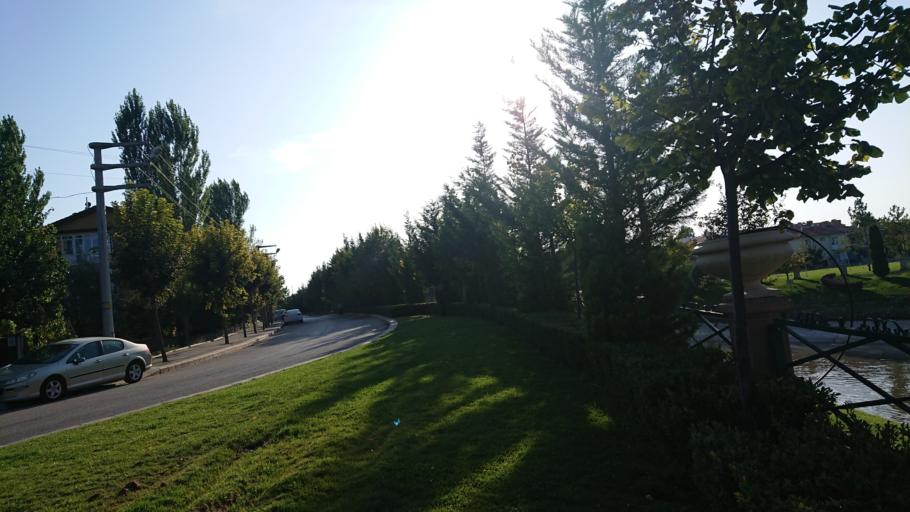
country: TR
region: Eskisehir
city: Eskisehir
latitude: 39.7676
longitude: 30.4921
